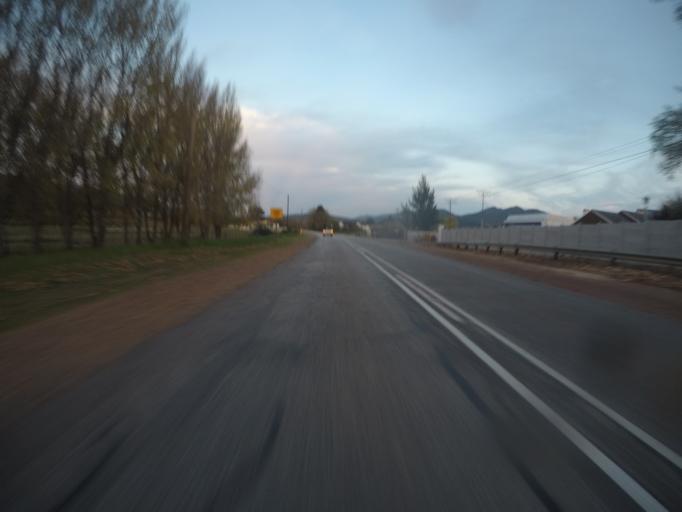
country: ZA
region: Western Cape
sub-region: Eden District Municipality
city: Plettenberg Bay
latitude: -33.7529
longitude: 23.4871
